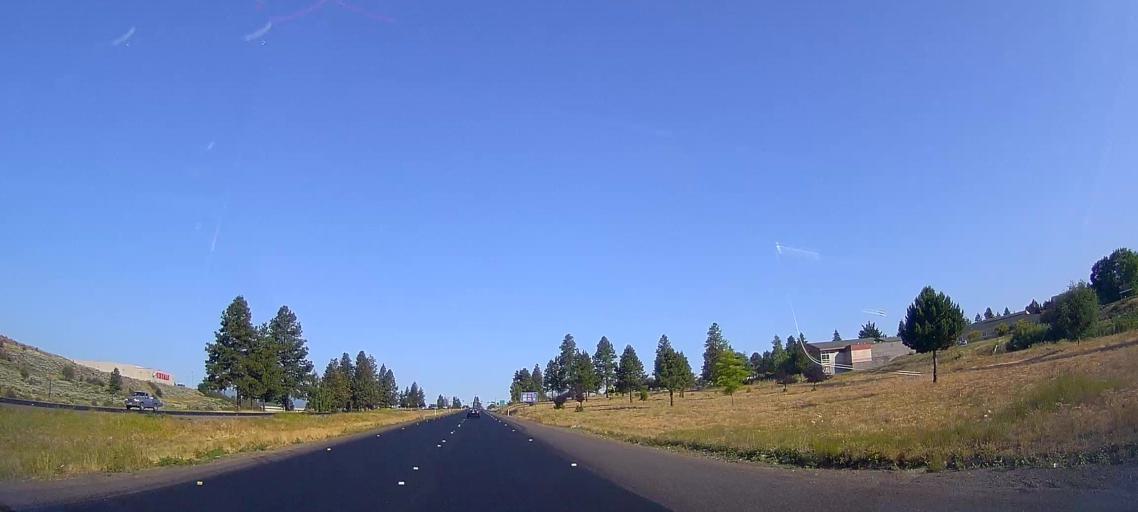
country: US
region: Oregon
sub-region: Klamath County
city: Klamath Falls
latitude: 42.2454
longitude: -121.7860
